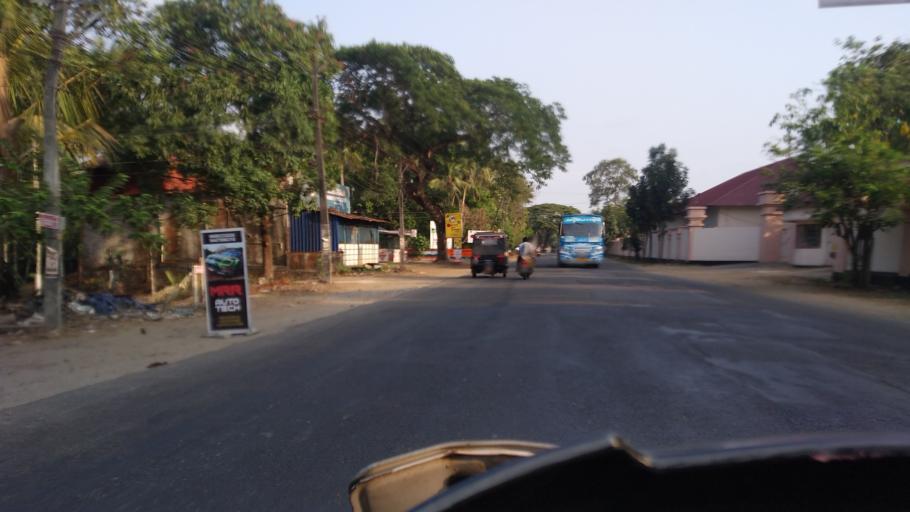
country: IN
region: Kerala
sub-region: Thrissur District
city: Thanniyam
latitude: 10.4262
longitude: 76.1021
